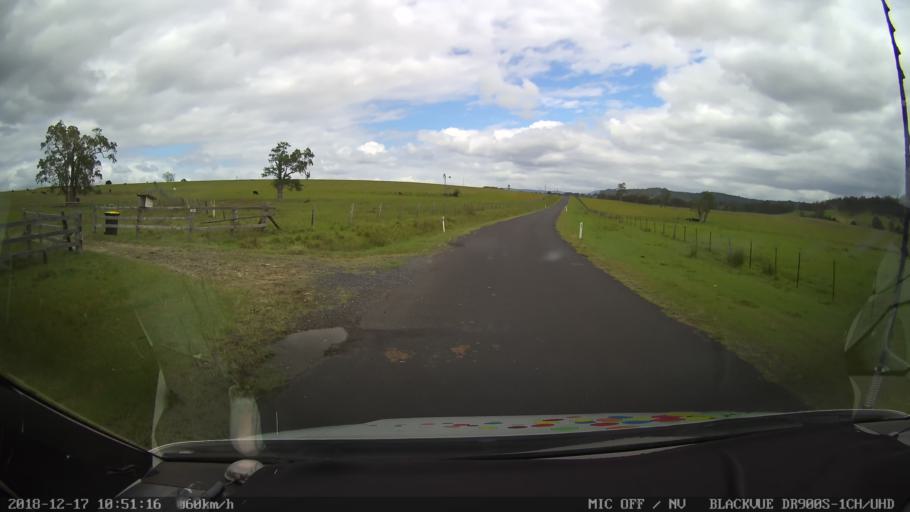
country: AU
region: New South Wales
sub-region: Tenterfield Municipality
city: Carrolls Creek
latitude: -28.8531
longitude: 152.5678
